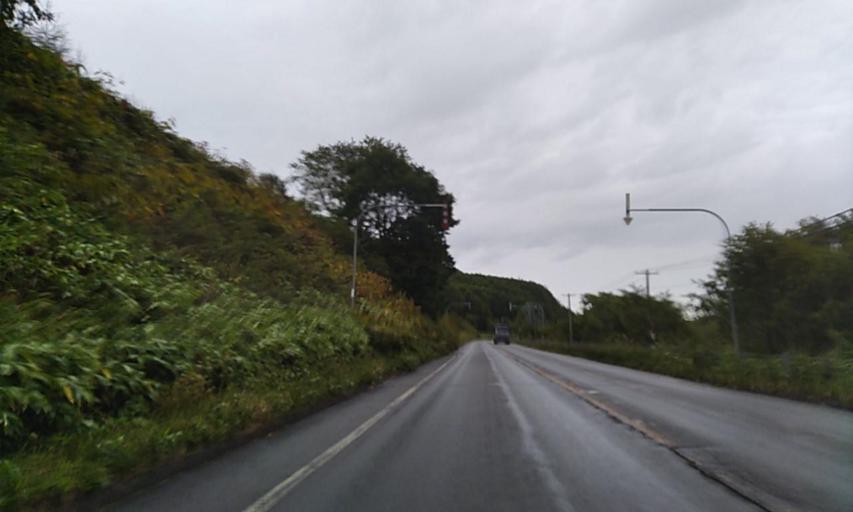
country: JP
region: Hokkaido
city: Mombetsu
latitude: 44.4877
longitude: 143.0771
